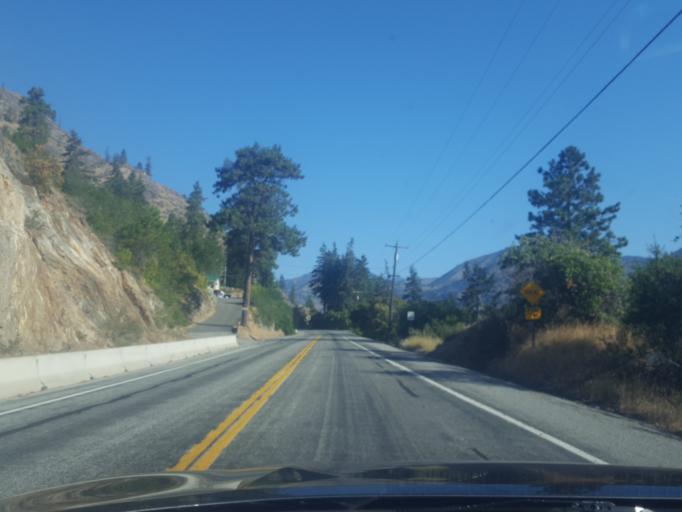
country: US
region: Washington
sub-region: Chelan County
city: Granite Falls
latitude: 47.9714
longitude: -120.2171
